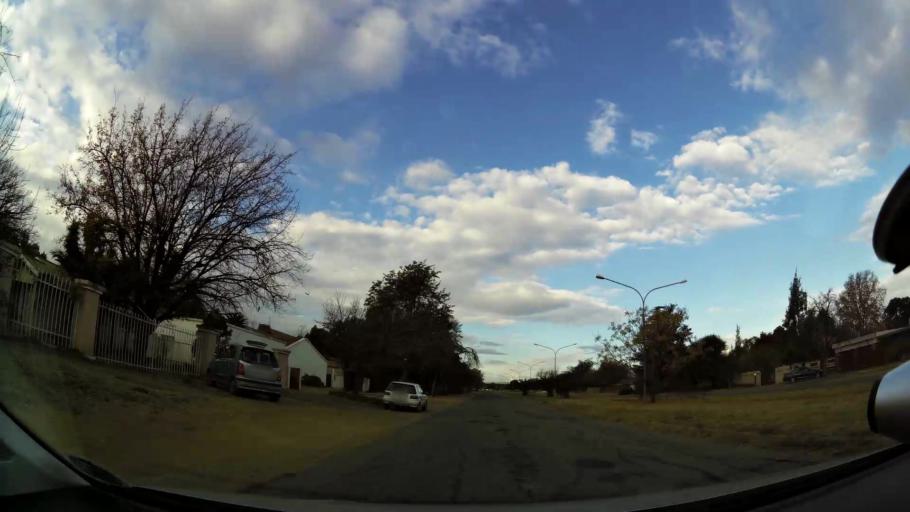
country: ZA
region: Orange Free State
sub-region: Lejweleputswa District Municipality
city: Welkom
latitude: -27.9888
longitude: 26.7246
